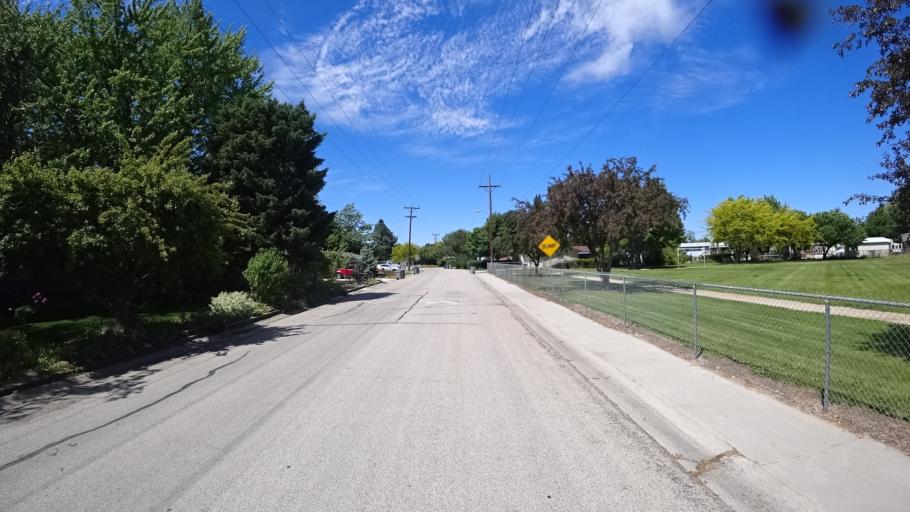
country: US
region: Idaho
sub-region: Ada County
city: Boise
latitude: 43.5752
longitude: -116.2264
